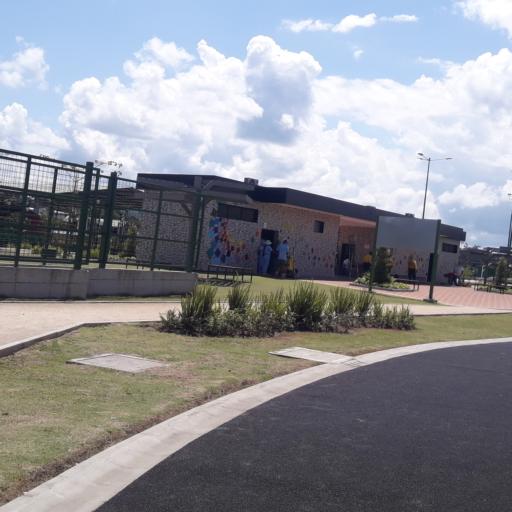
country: EC
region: Napo
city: Tena
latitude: -0.9869
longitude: -77.8195
